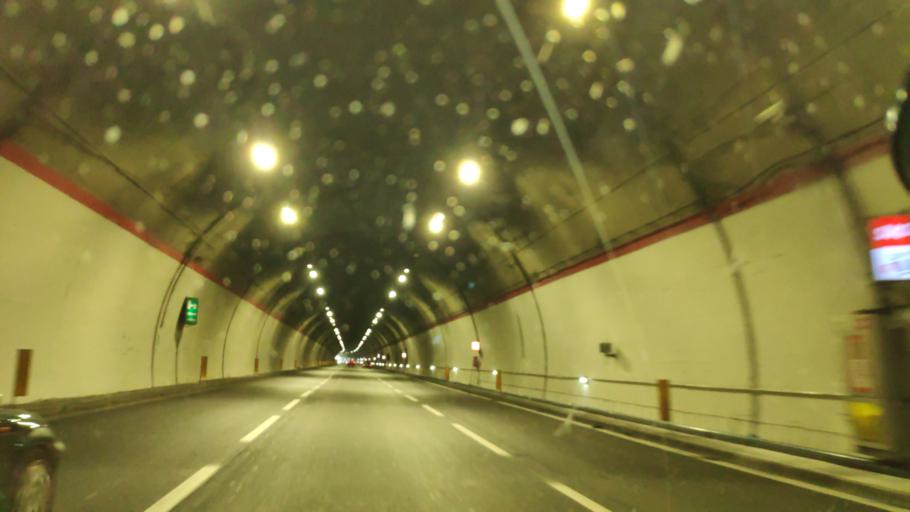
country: IT
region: Campania
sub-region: Provincia di Salerno
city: Fuorni
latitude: 40.6679
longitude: 14.8582
